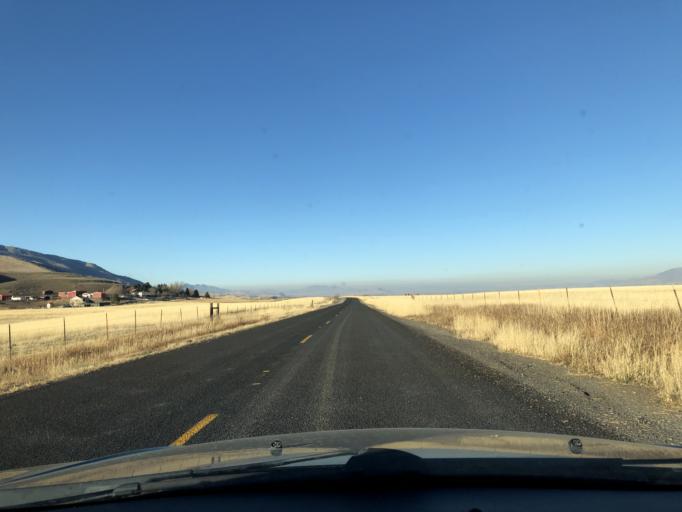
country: US
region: Utah
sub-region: Cache County
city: Wellsville
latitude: 41.5890
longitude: -111.9264
